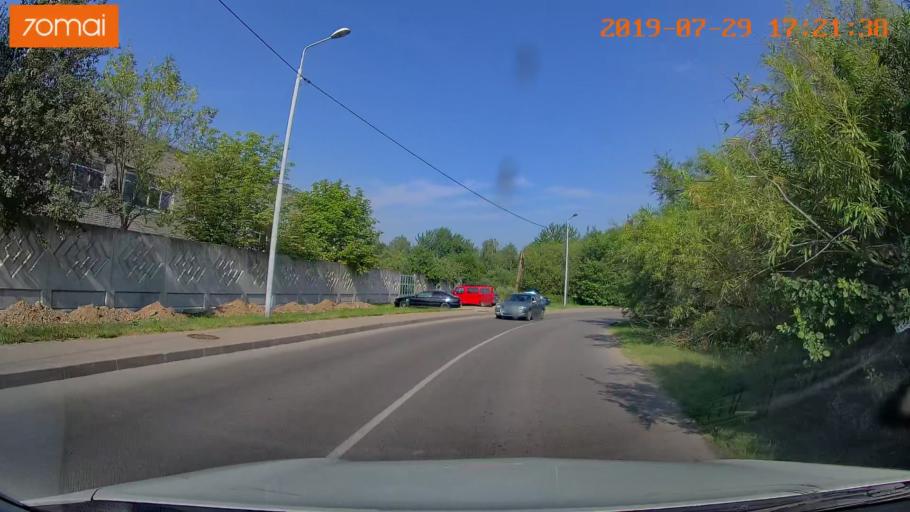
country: RU
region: Kaliningrad
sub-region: Gorod Kaliningrad
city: Kaliningrad
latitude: 54.7704
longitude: 20.4313
